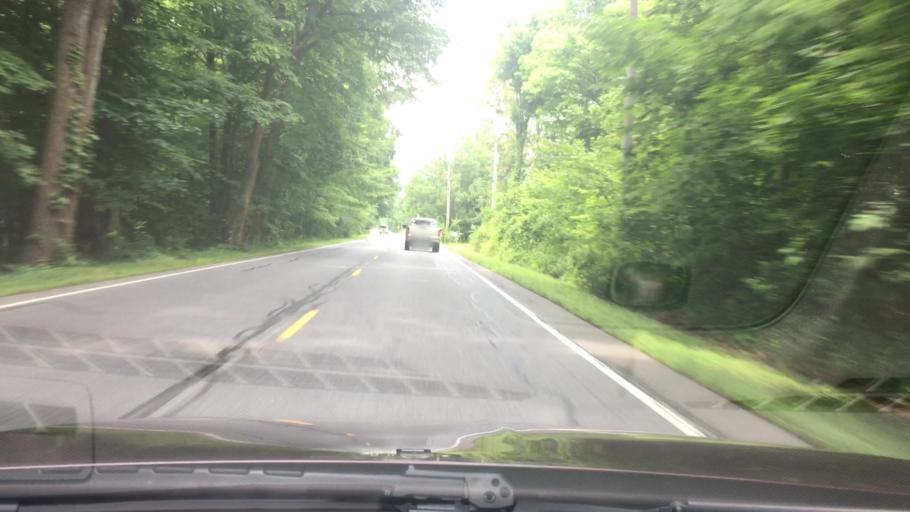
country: US
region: New York
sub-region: Dutchess County
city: Hillside Lake
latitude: 41.6454
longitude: -73.7785
